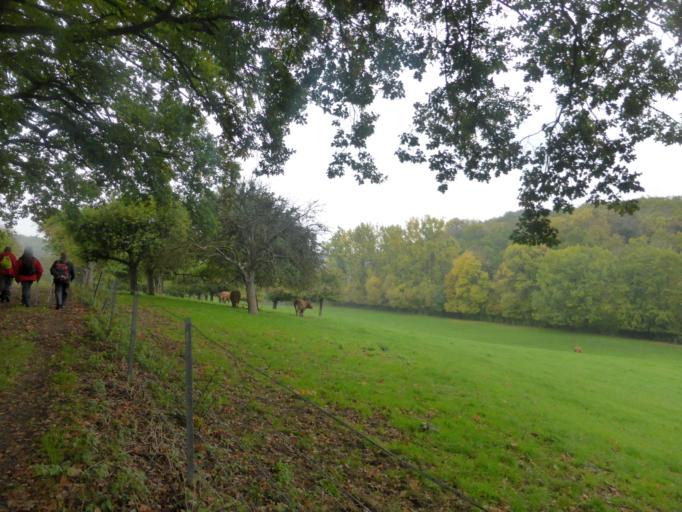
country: LU
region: Grevenmacher
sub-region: Canton de Grevenmacher
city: Mertert
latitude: 49.7091
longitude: 6.4690
